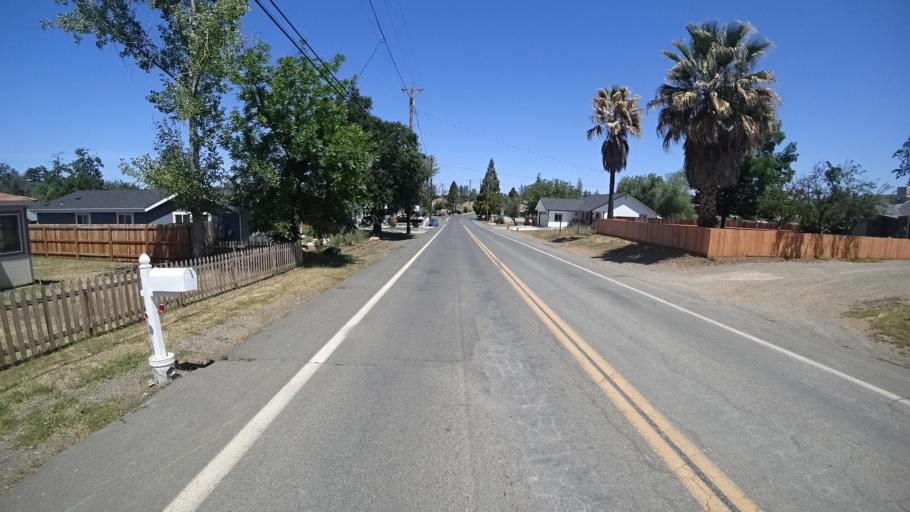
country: US
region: California
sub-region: Lake County
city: Lower Lake
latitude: 38.9125
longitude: -122.6093
